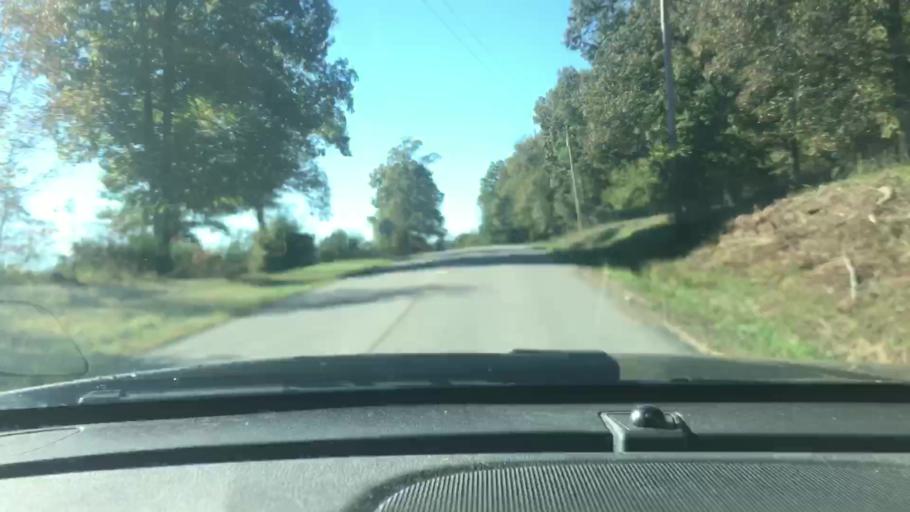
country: US
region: Tennessee
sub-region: Dickson County
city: Charlotte
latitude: 36.1801
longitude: -87.2934
